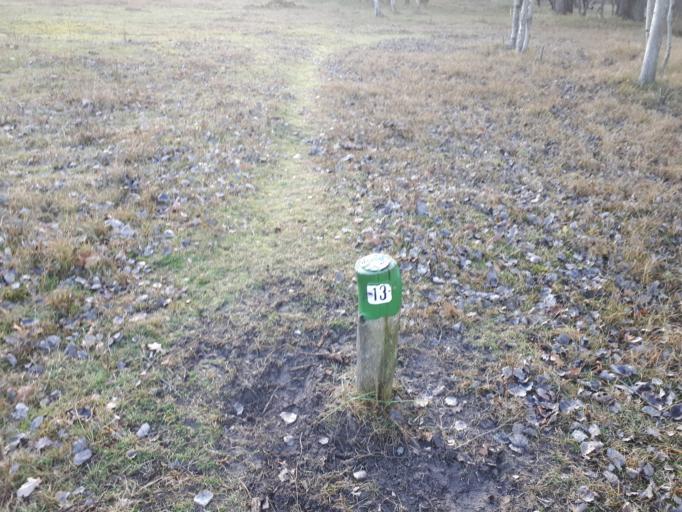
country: NL
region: South Holland
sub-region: Gemeente Wassenaar
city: Wassenaar
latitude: 52.1425
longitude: 4.3623
